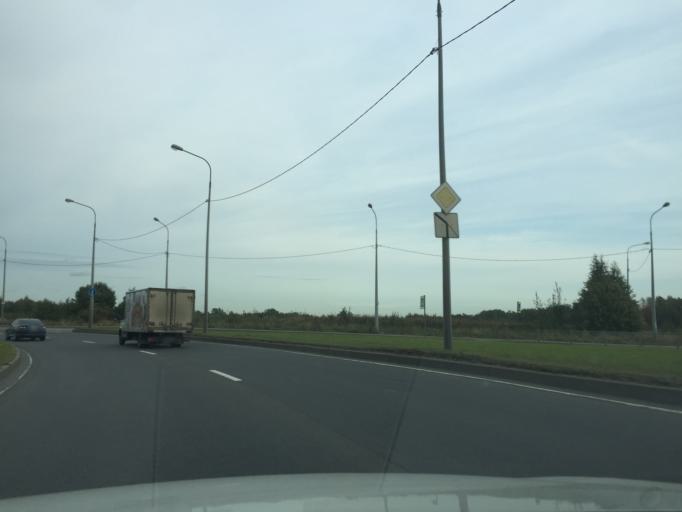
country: RU
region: St.-Petersburg
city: Krasnogvargeisky
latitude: 59.9859
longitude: 30.4595
